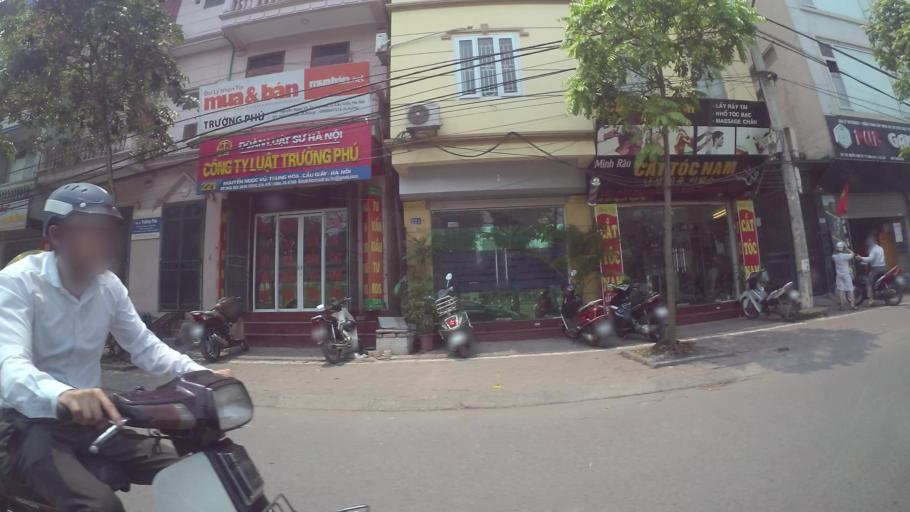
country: VN
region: Ha Noi
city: Cau Giay
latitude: 21.0141
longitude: 105.8055
